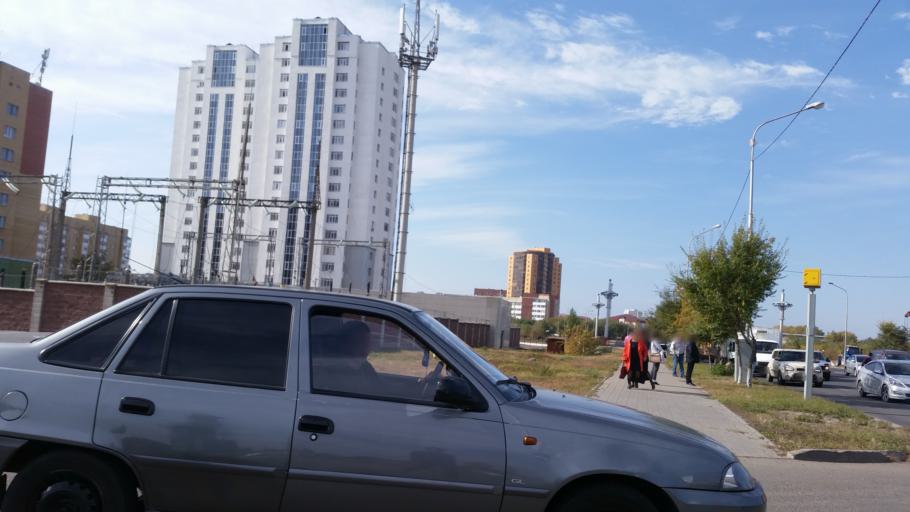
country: KZ
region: Astana Qalasy
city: Astana
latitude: 51.1637
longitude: 71.4799
